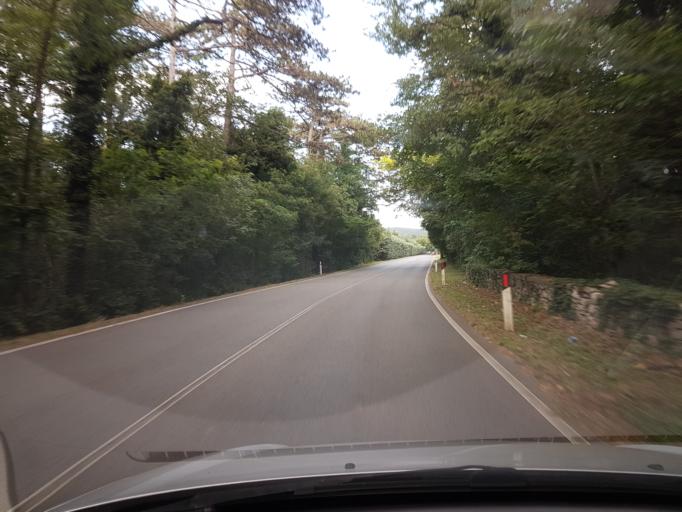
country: IT
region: Friuli Venezia Giulia
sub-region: Provincia di Trieste
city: Villa Opicina
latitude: 45.6778
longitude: 13.8137
